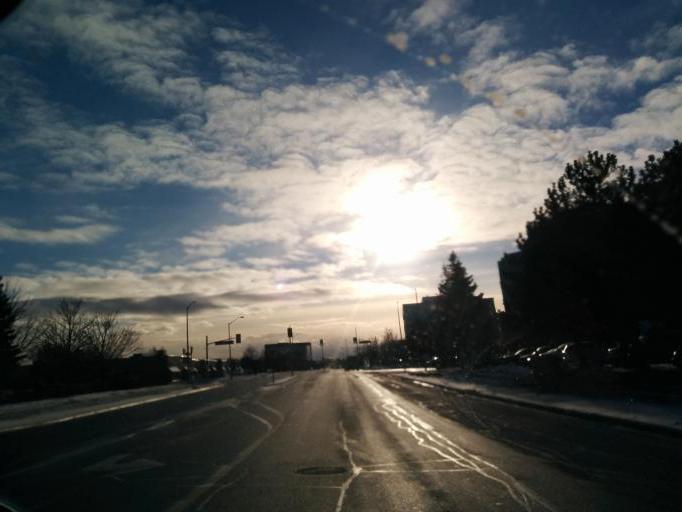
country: CA
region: Ontario
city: Etobicoke
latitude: 43.6635
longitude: -79.5976
